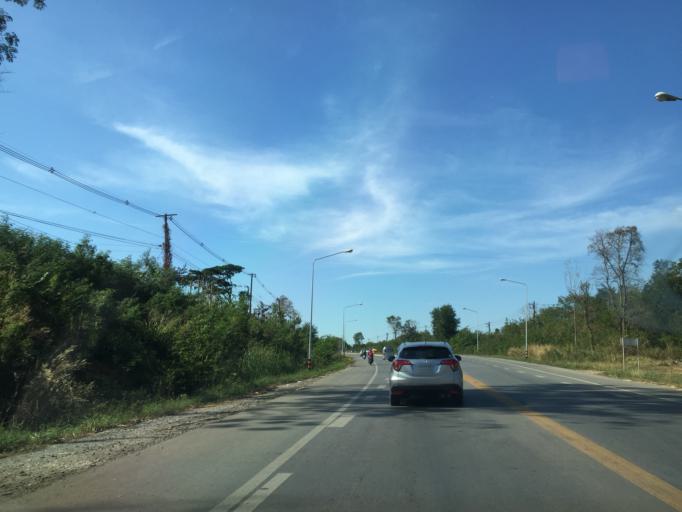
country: TH
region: Loei
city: Wang Saphung
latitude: 17.2927
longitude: 101.8202
